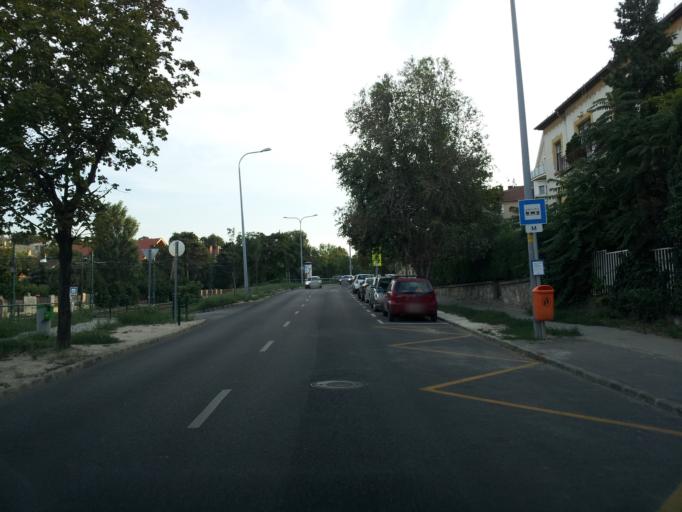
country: HU
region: Budapest
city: Budapest XII. keruelet
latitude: 47.4896
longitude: 19.0095
